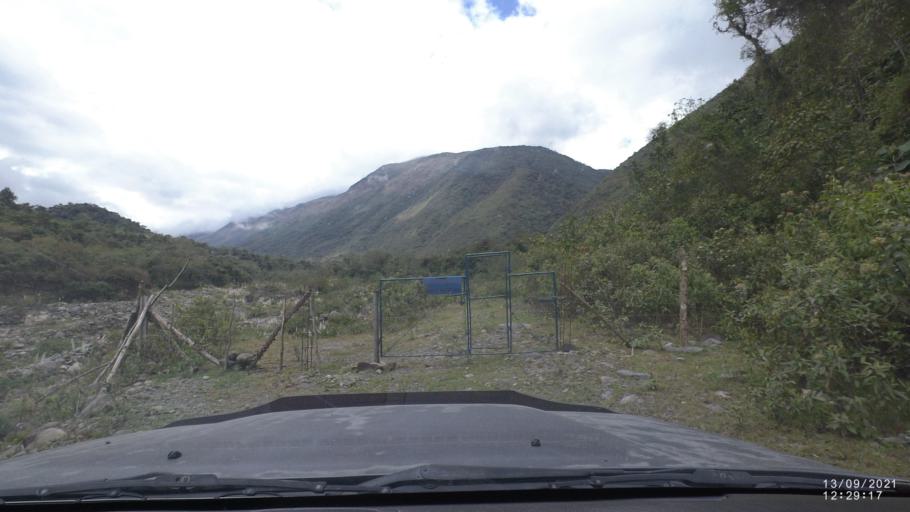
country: BO
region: Cochabamba
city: Colomi
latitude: -17.2598
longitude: -65.8151
